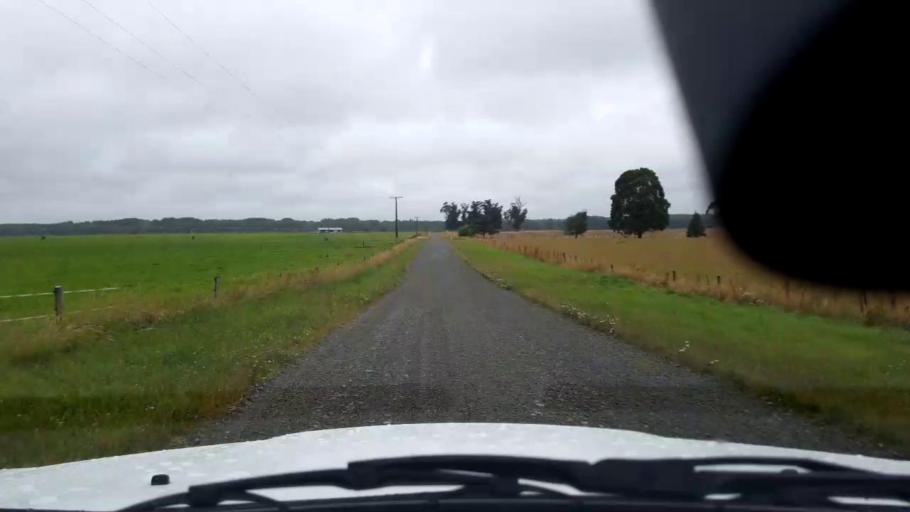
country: NZ
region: Canterbury
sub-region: Timaru District
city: Pleasant Point
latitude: -44.2464
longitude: 171.2009
